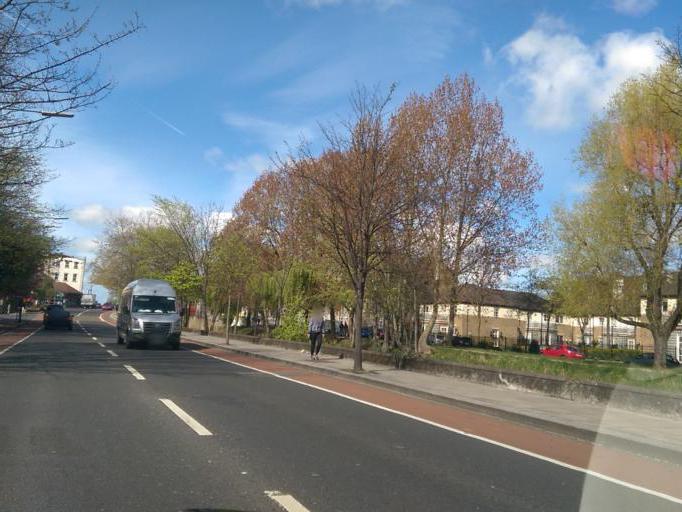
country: IE
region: Leinster
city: Rathmines
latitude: 53.3301
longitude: -6.2620
